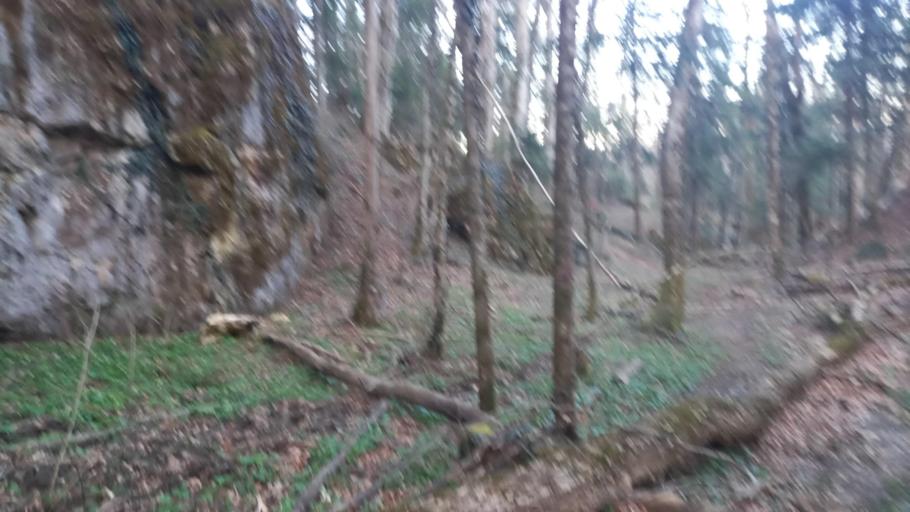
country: RU
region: Adygeya
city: Kamennomostskiy
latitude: 44.1004
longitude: 40.0788
